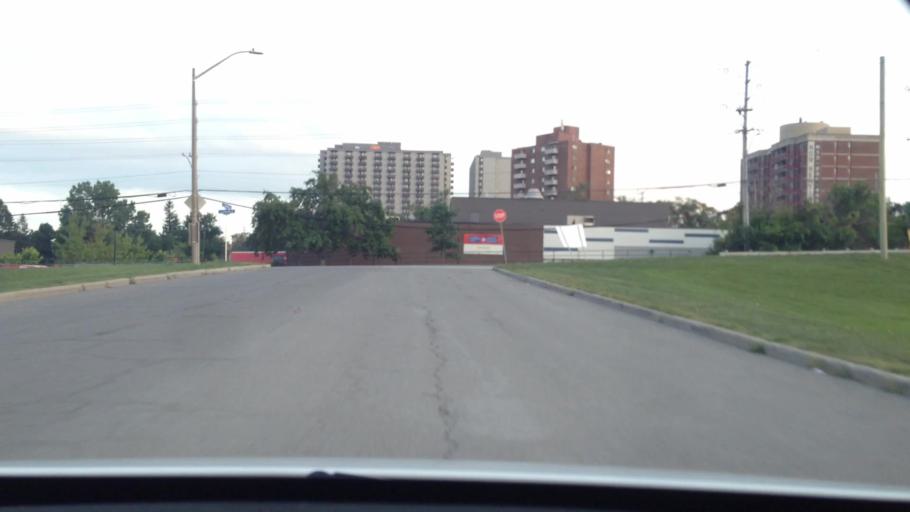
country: CA
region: Ontario
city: Ottawa
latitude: 45.4024
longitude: -75.6233
